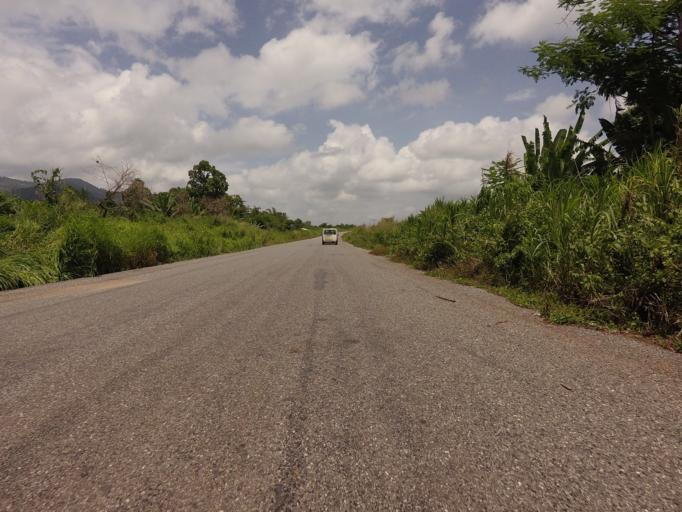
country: GH
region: Volta
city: Kpandu
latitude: 6.8446
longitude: 0.3904
